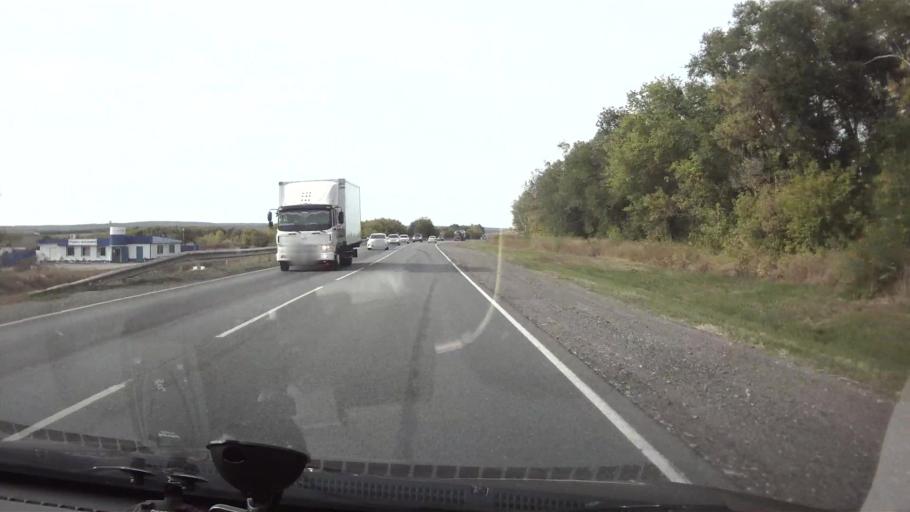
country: RU
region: Saratov
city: Tersa
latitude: 52.0883
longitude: 47.5482
